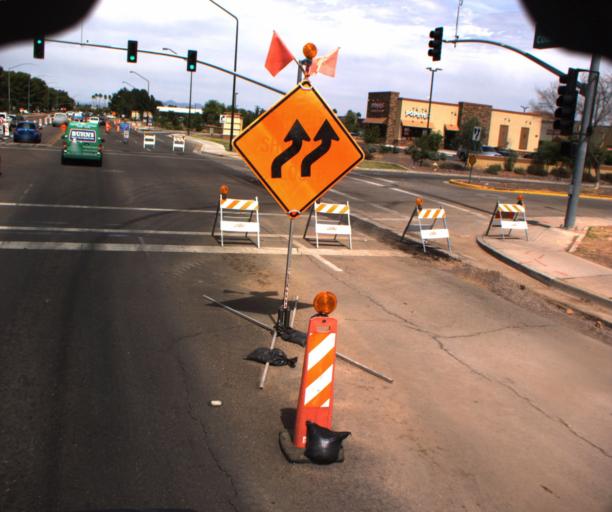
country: US
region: Arizona
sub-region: Maricopa County
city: San Carlos
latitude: 33.3726
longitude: -111.8422
